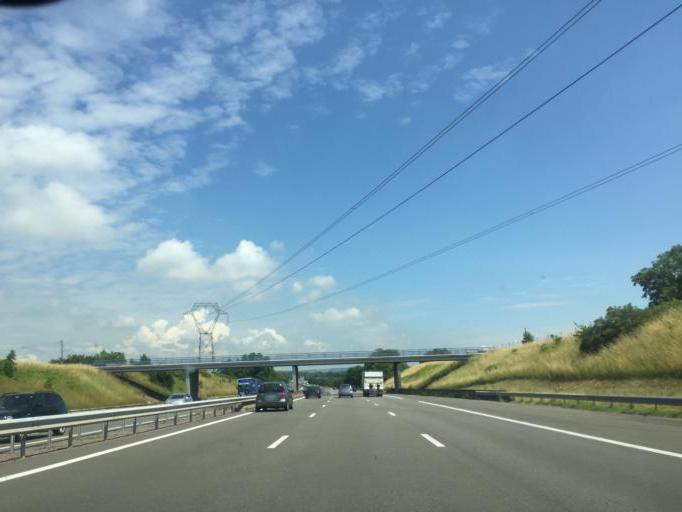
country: FR
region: Bourgogne
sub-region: Departement de Saone-et-Loire
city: Saint-Martin-Belle-Roche
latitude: 46.4273
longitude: 4.8685
